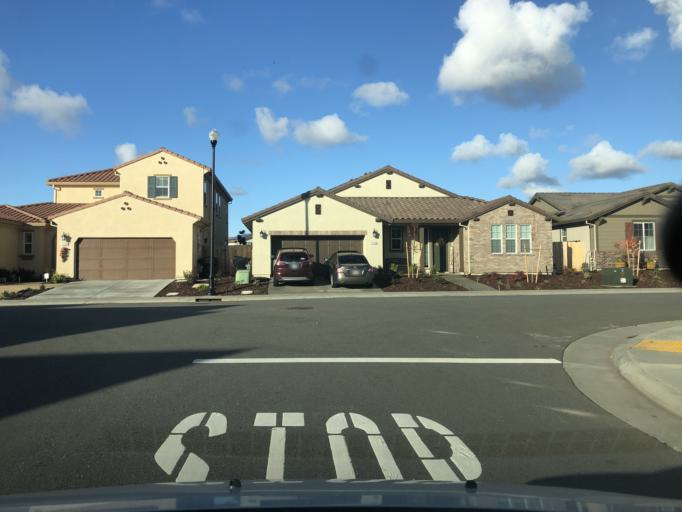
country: US
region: California
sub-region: Sacramento County
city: Antelope
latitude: 38.7744
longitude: -121.3819
